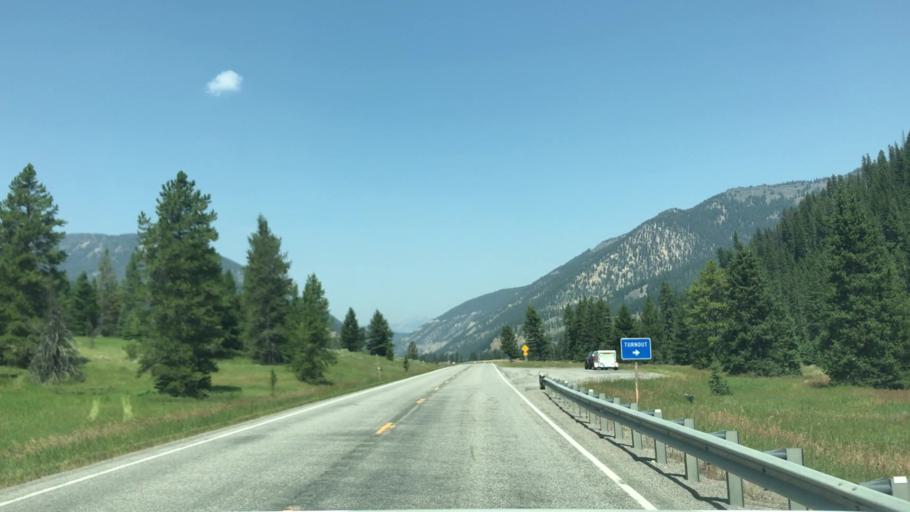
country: US
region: Montana
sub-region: Gallatin County
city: Big Sky
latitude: 45.0900
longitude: -111.2133
